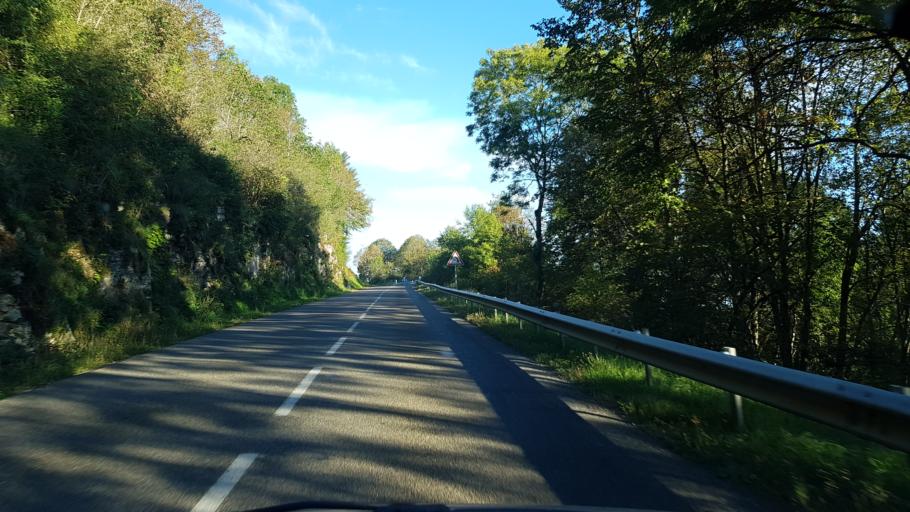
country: FR
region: Franche-Comte
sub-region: Departement du Jura
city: Lons-le-Saunier
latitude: 46.6354
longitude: 5.5409
